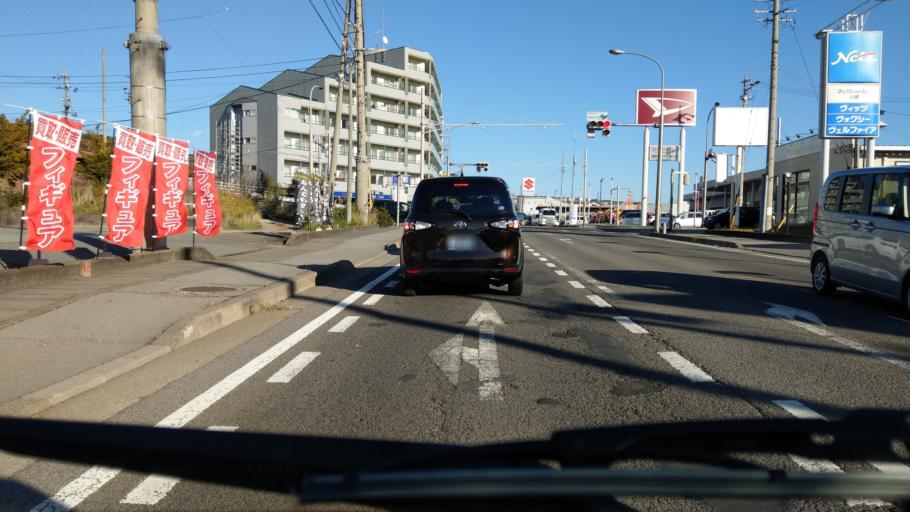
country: JP
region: Nagano
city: Komoro
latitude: 36.3377
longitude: 138.4079
